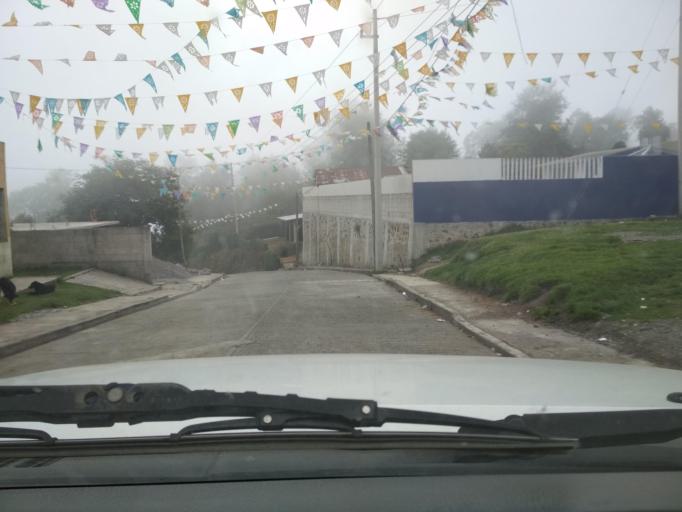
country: MX
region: Veracruz
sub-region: La Perla
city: Chilapa
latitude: 18.9992
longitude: -97.1610
